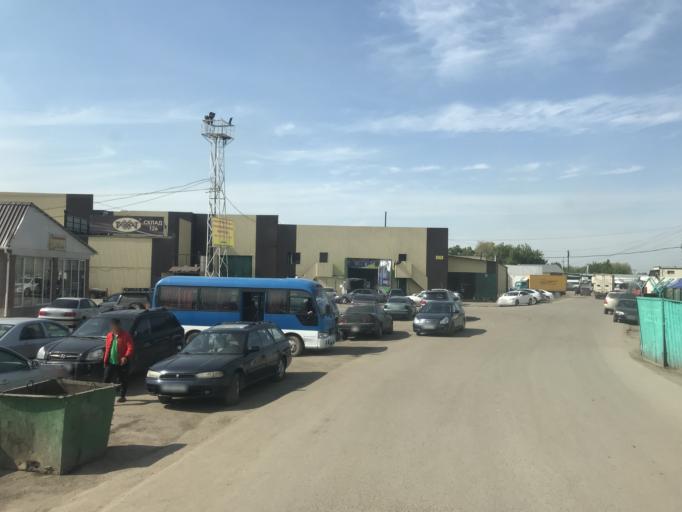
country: KZ
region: Almaty Oblysy
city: Burunday
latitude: 43.2326
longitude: 76.7698
